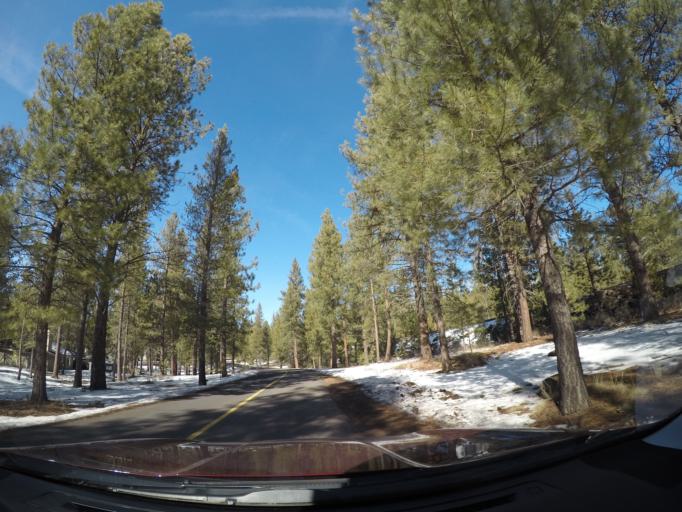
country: US
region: Oregon
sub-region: Deschutes County
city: Sunriver
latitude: 43.8720
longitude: -121.4310
